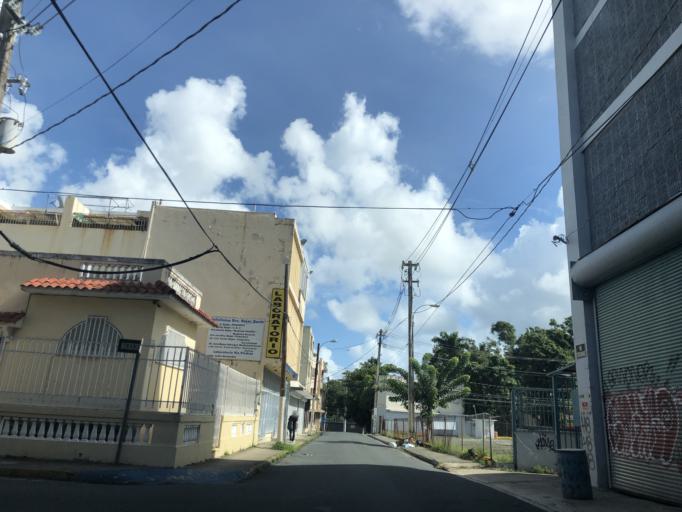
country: PR
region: Trujillo Alto
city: Trujillo Alto
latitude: 18.3991
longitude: -66.0499
